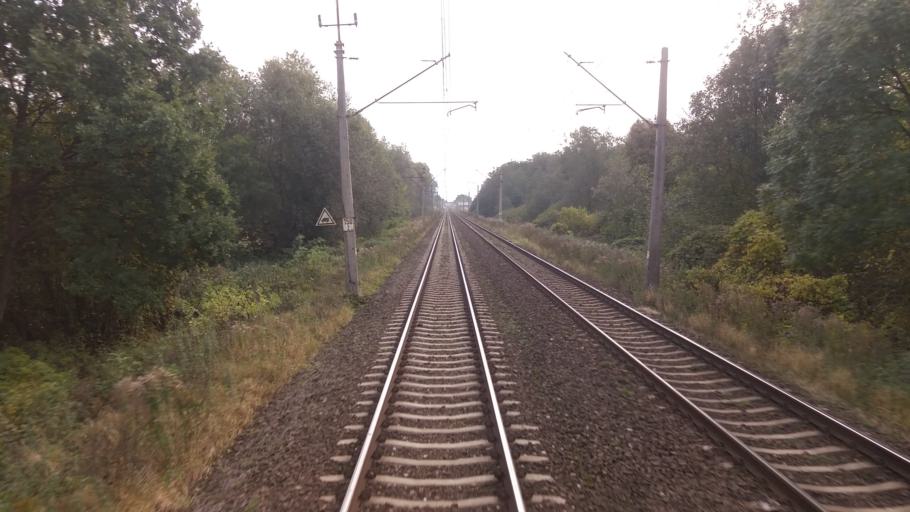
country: PL
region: West Pomeranian Voivodeship
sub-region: Powiat stargardzki
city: Dolice
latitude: 53.2246
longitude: 15.1464
